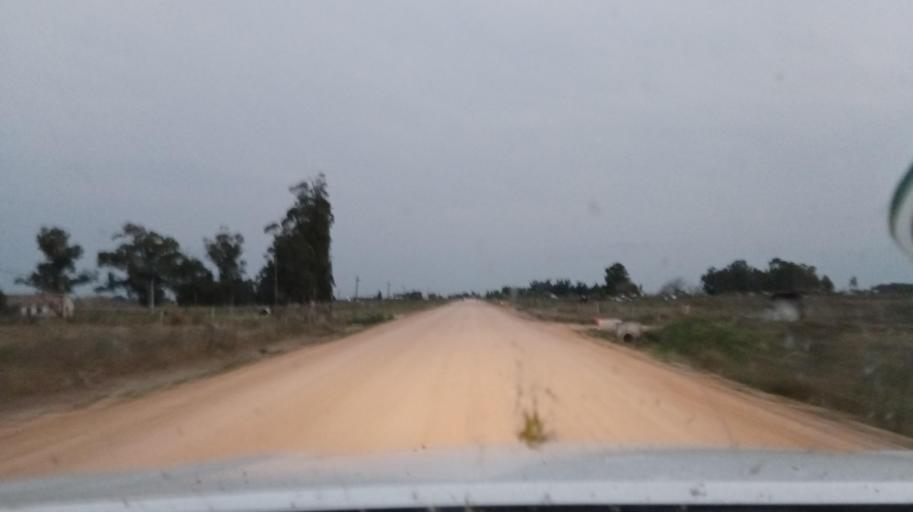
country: UY
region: Canelones
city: Santa Rosa
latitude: -34.5325
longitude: -56.0992
